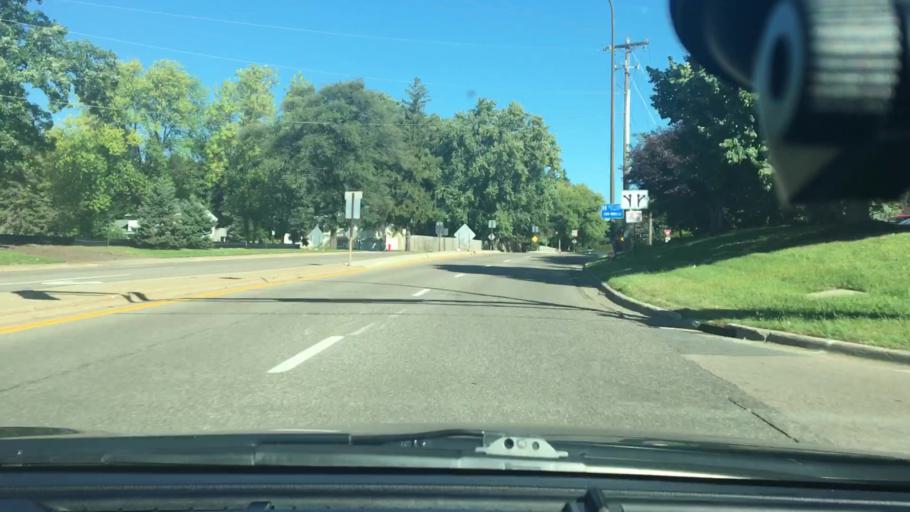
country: US
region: Minnesota
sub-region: Hennepin County
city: Minnetonka Mills
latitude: 44.9731
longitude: -93.4462
